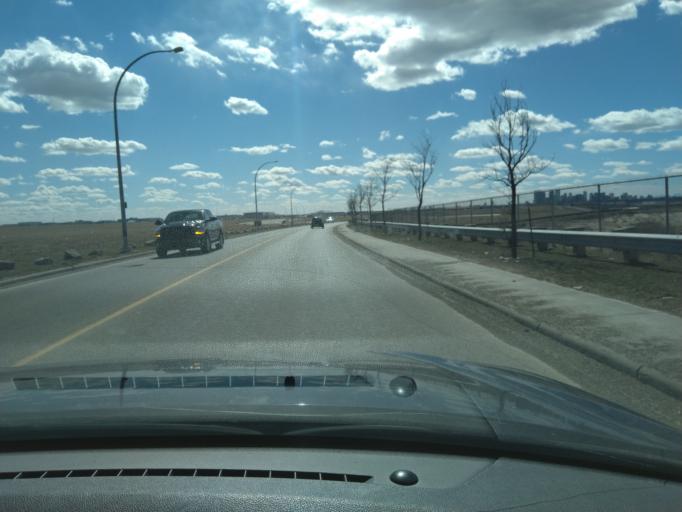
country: CA
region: Alberta
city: Calgary
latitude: 51.1156
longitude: -114.0297
